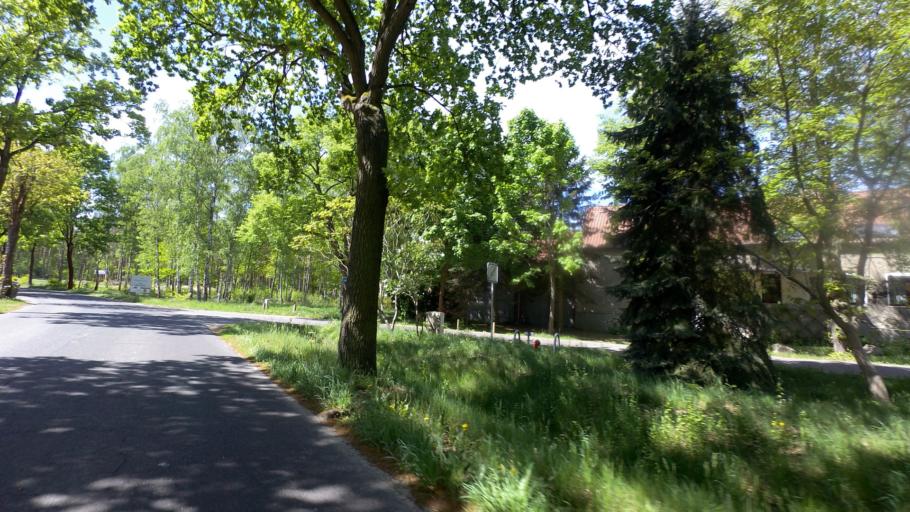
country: DE
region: Brandenburg
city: Michendorf
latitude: 52.2442
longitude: 13.0742
